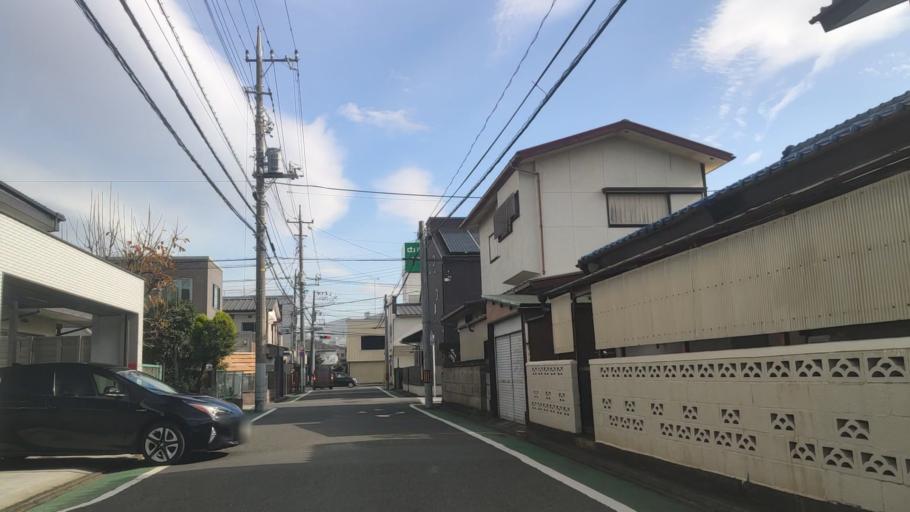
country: JP
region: Kanagawa
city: Atsugi
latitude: 35.4339
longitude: 139.3645
